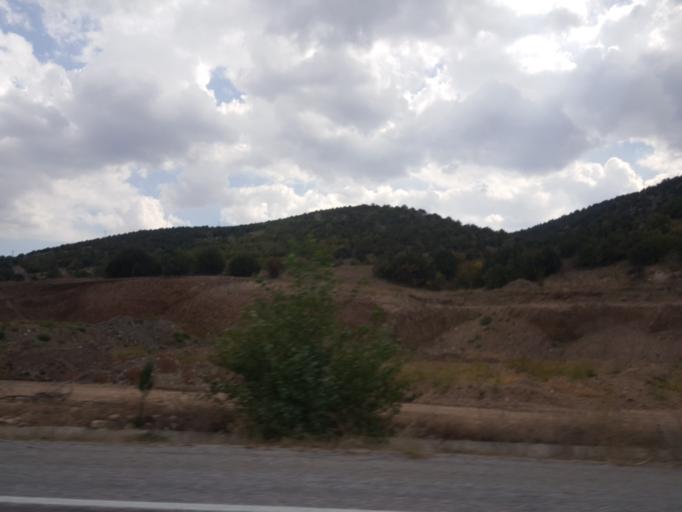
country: TR
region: Yozgat
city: Aydincik
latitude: 40.1870
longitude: 35.3984
